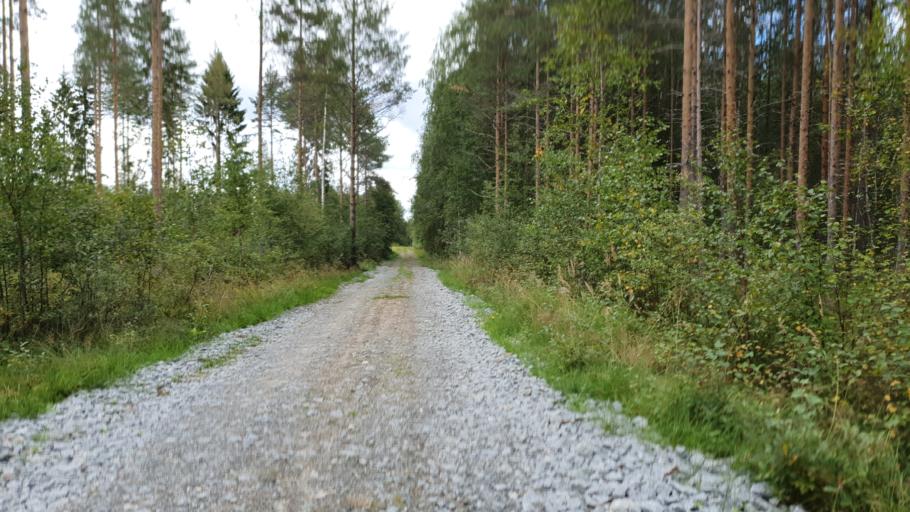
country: FI
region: Kainuu
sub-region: Kehys-Kainuu
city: Kuhmo
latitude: 64.1326
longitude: 29.4499
